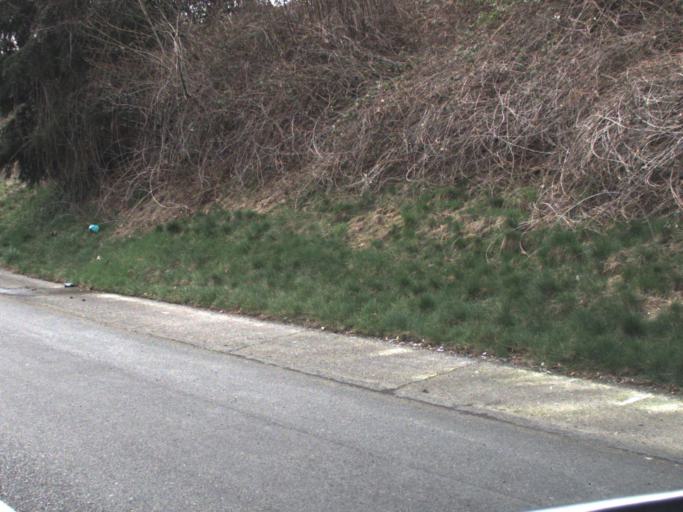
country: US
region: Washington
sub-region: King County
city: Kent
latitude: 47.3900
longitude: -122.2793
